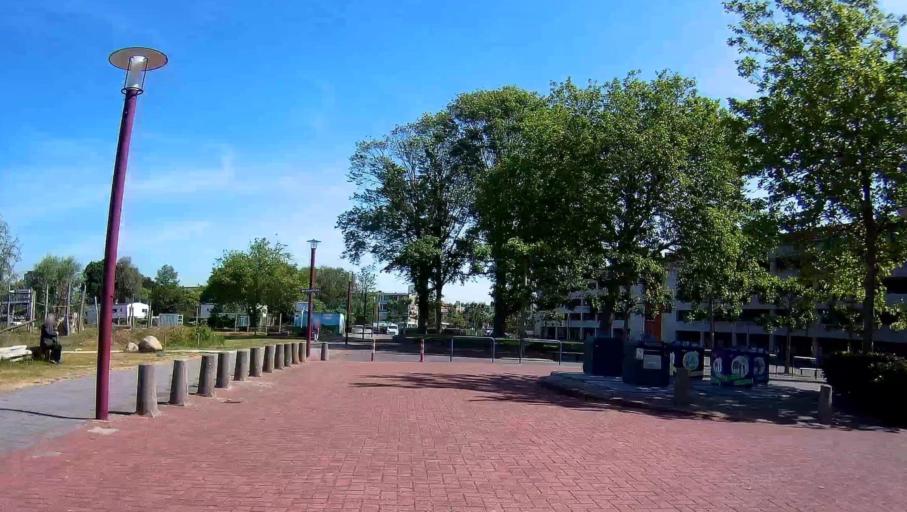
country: NL
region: South Holland
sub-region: Gemeente Schiedam
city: Schiedam
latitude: 51.9176
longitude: 4.3824
